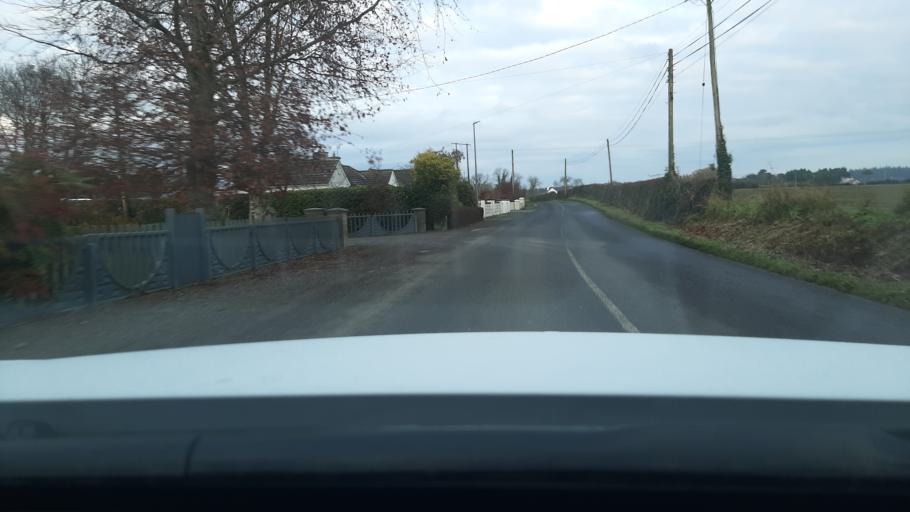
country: IE
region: Leinster
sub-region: Kildare
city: Rathangan
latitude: 53.2289
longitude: -7.0072
